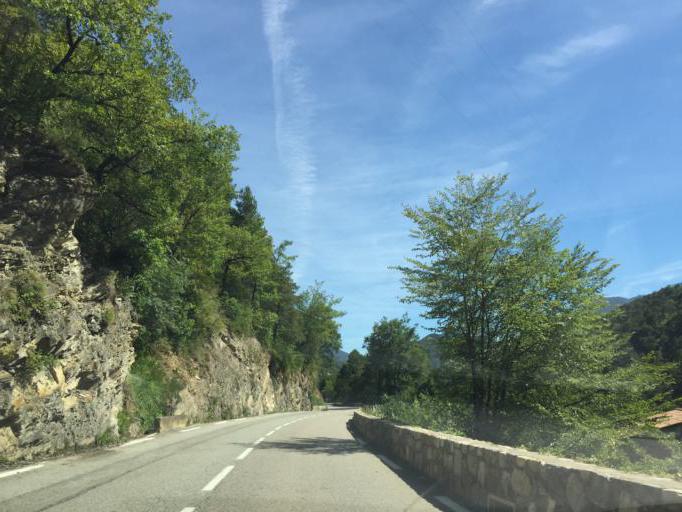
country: FR
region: Provence-Alpes-Cote d'Azur
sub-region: Departement des Alpes-Maritimes
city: Gilette
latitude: 43.9718
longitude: 7.1468
